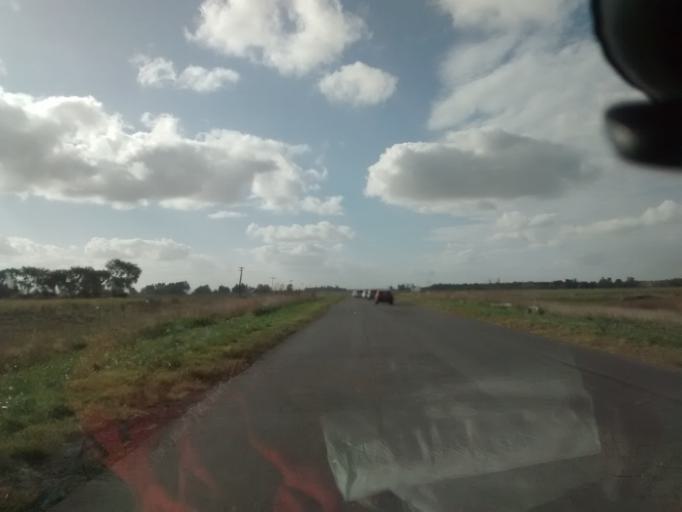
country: AR
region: Buenos Aires
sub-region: Partido de Ayacucho
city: Ayacucho
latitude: -37.1915
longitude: -58.5102
